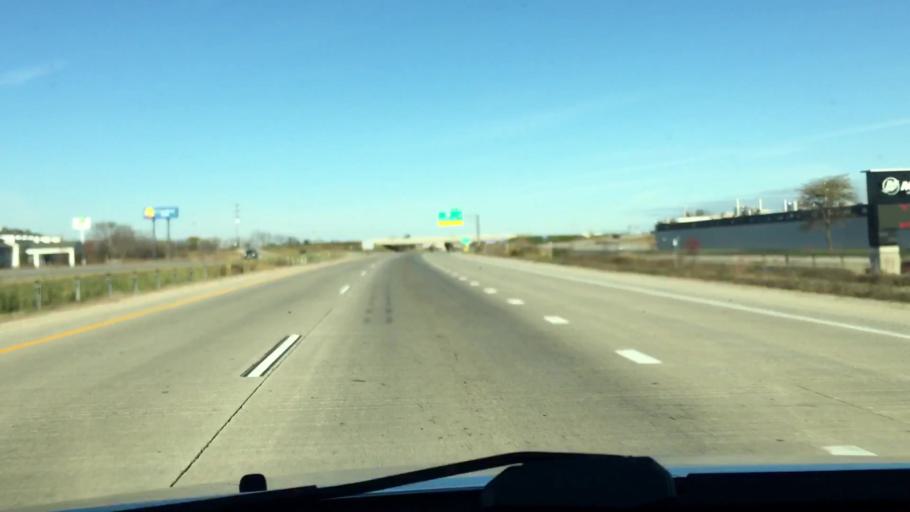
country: US
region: Wisconsin
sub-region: Fond du Lac County
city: Fond du Lac
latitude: 43.7553
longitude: -88.4706
